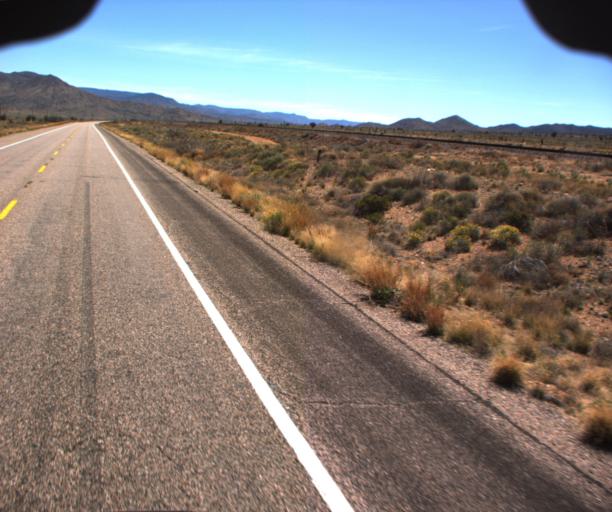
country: US
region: Arizona
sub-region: Mohave County
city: New Kingman-Butler
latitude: 35.4115
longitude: -113.7804
